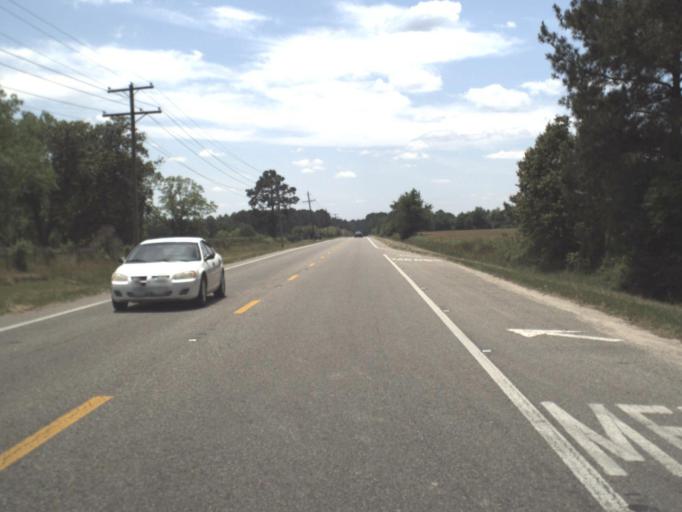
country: US
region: Florida
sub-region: Calhoun County
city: Blountstown
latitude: 30.5459
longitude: -85.1295
